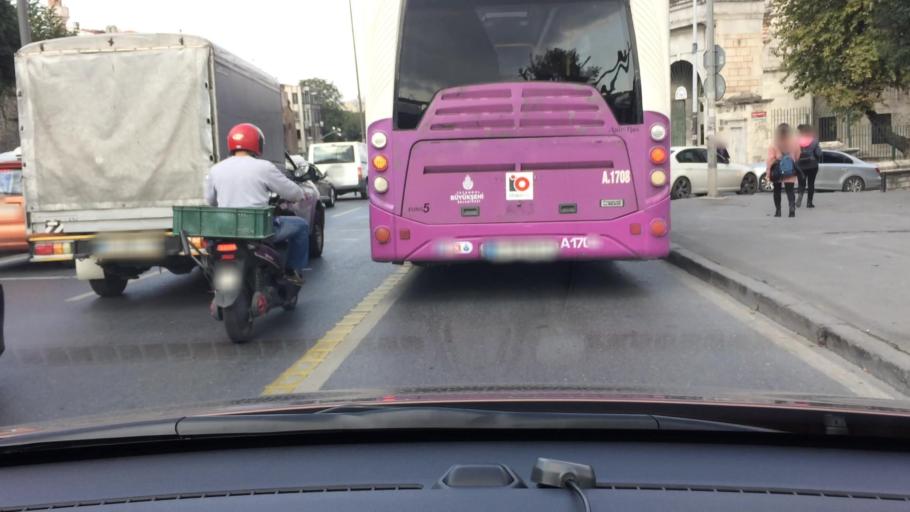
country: TR
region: Istanbul
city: Istanbul
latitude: 41.0189
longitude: 28.9583
